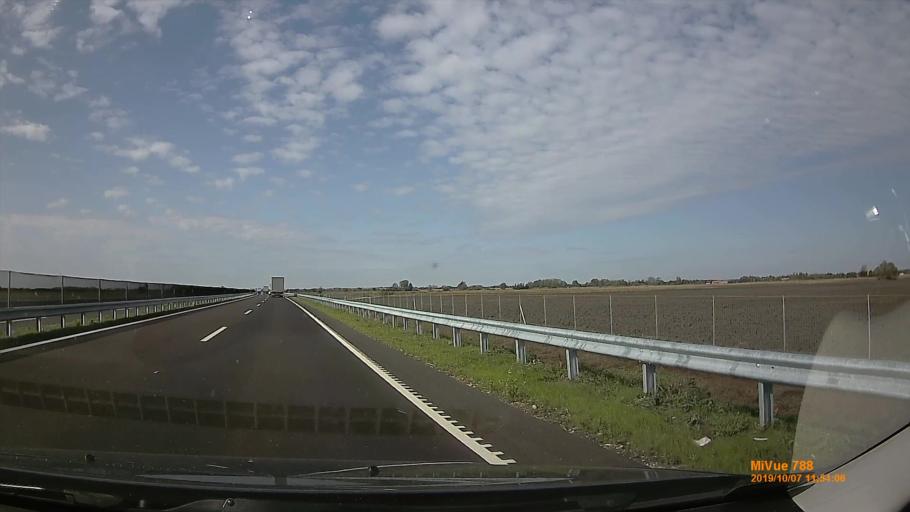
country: HU
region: Bekes
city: Szarvas
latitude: 46.8197
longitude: 20.5974
